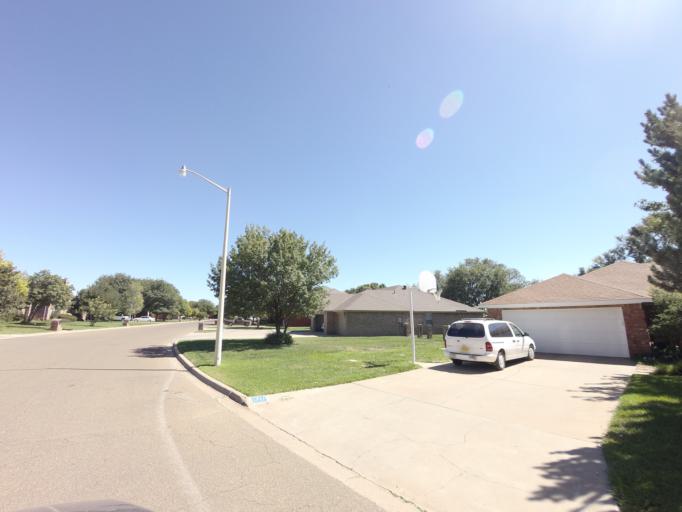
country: US
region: New Mexico
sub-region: Curry County
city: Clovis
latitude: 34.4431
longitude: -103.1849
